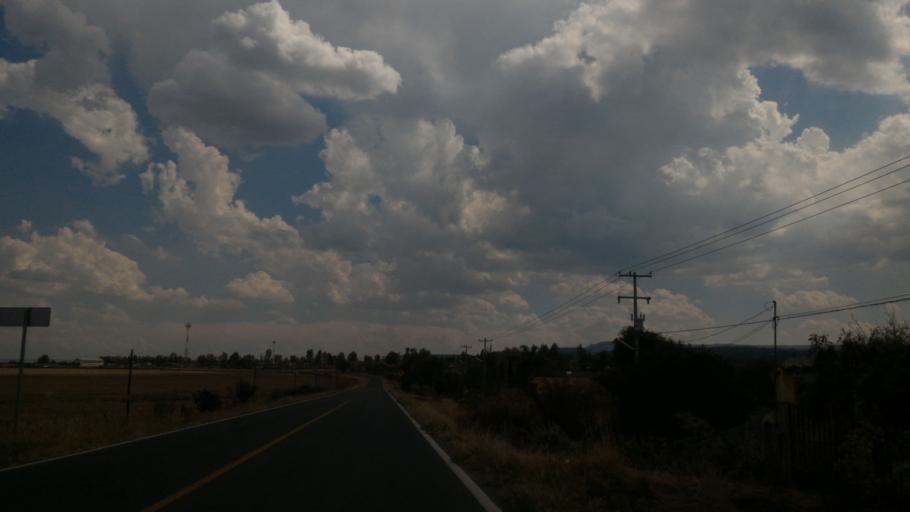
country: MX
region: Guanajuato
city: Ciudad Manuel Doblado
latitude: 20.8102
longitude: -101.9978
